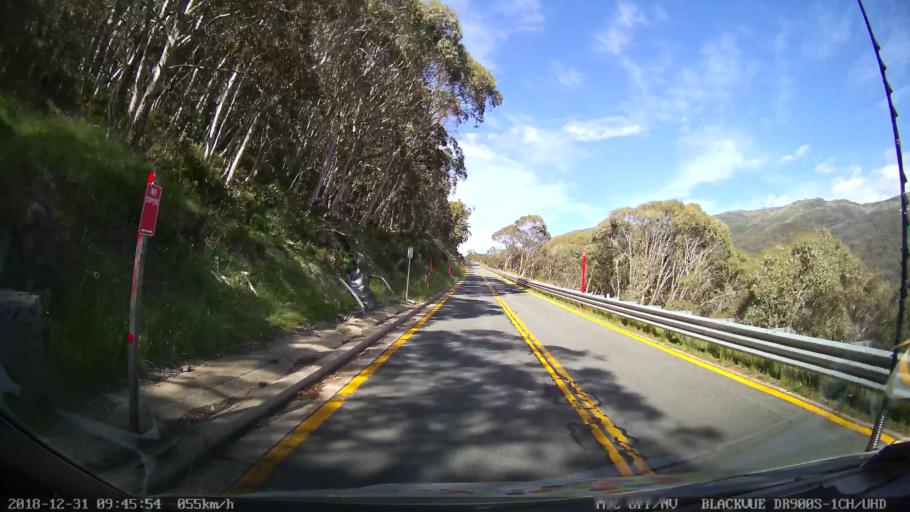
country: AU
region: New South Wales
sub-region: Snowy River
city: Jindabyne
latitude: -36.5017
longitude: 148.3141
